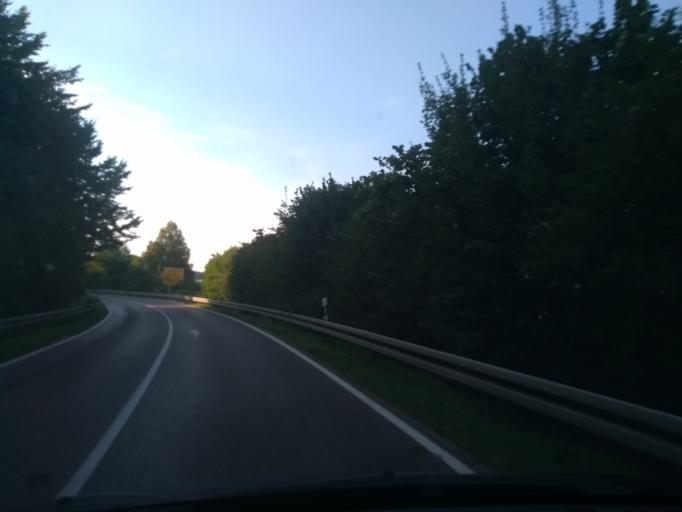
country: DE
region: Bavaria
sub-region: Upper Bavaria
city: Markt Indersdorf
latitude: 48.3666
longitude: 11.3810
